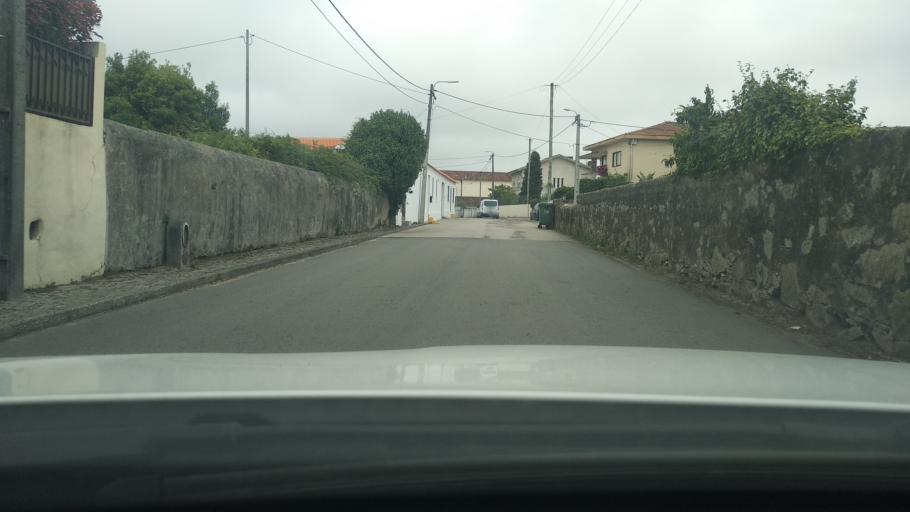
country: PT
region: Aveiro
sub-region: Espinho
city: Souto
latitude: 40.9889
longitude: -8.6252
